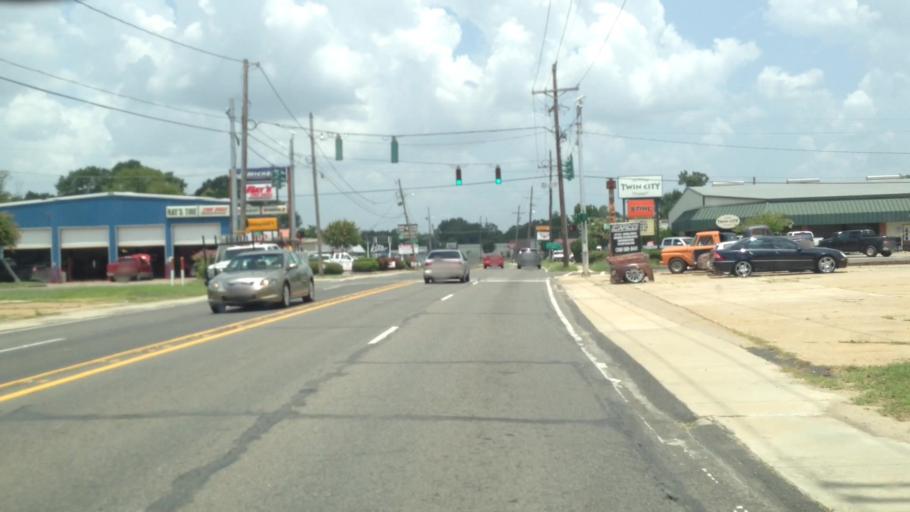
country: US
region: Louisiana
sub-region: Ouachita Parish
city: West Monroe
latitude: 32.5146
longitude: -92.1376
